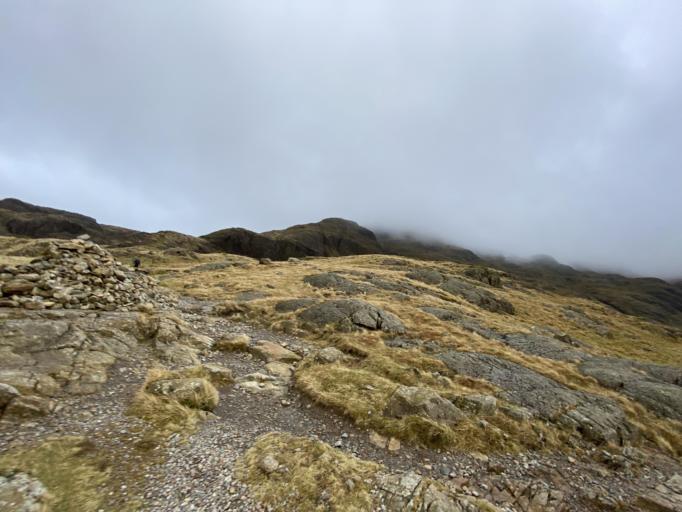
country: GB
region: England
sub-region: Cumbria
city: Keswick
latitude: 54.4748
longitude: -3.2050
